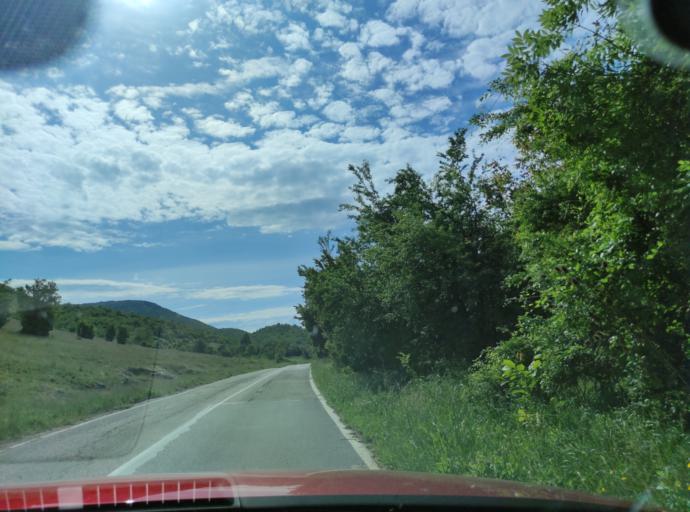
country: BG
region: Montana
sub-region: Obshtina Chiprovtsi
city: Chiprovtsi
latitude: 43.4907
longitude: 22.8083
